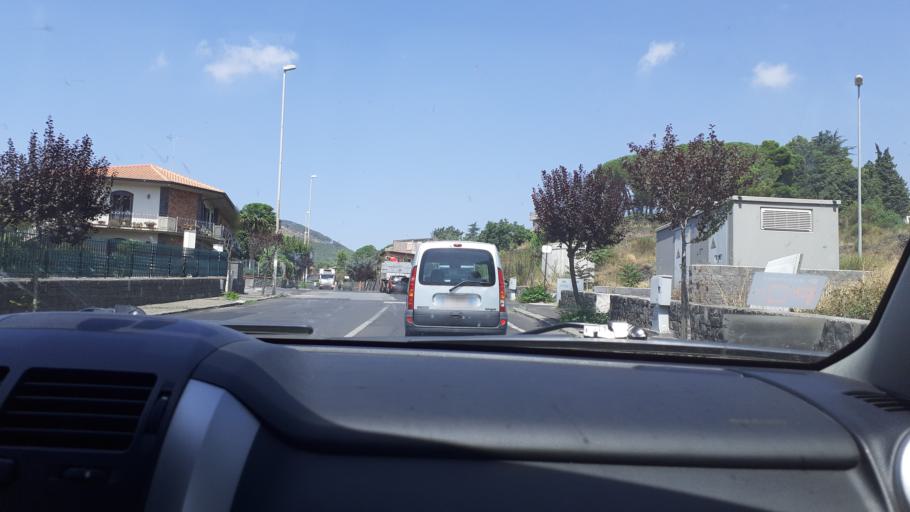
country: IT
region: Sicily
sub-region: Catania
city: Nicolosi
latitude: 37.6160
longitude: 15.0336
